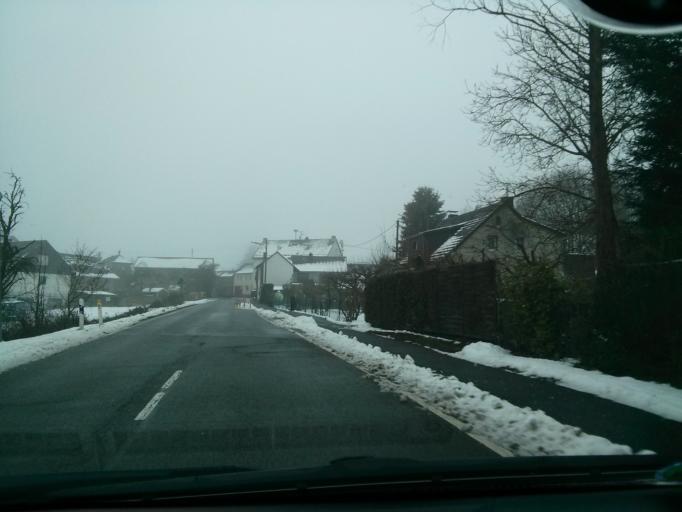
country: DE
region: Rheinland-Pfalz
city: Berg
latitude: 50.5657
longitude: 6.9676
